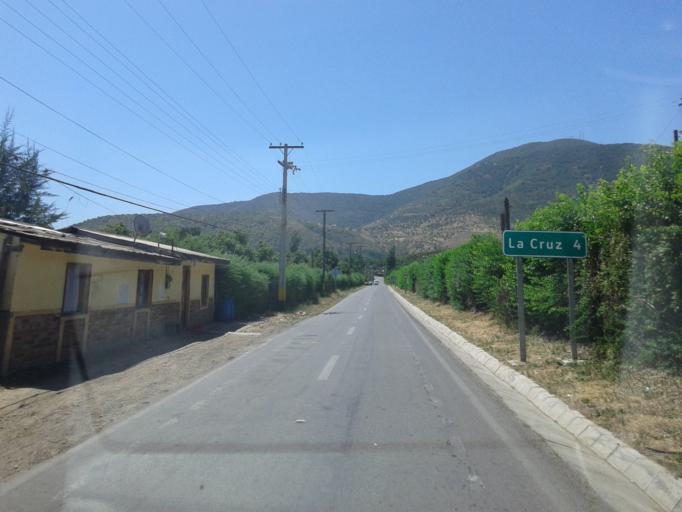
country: CL
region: Valparaiso
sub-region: Provincia de Quillota
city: Hacienda La Calera
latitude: -32.8400
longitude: -71.1932
